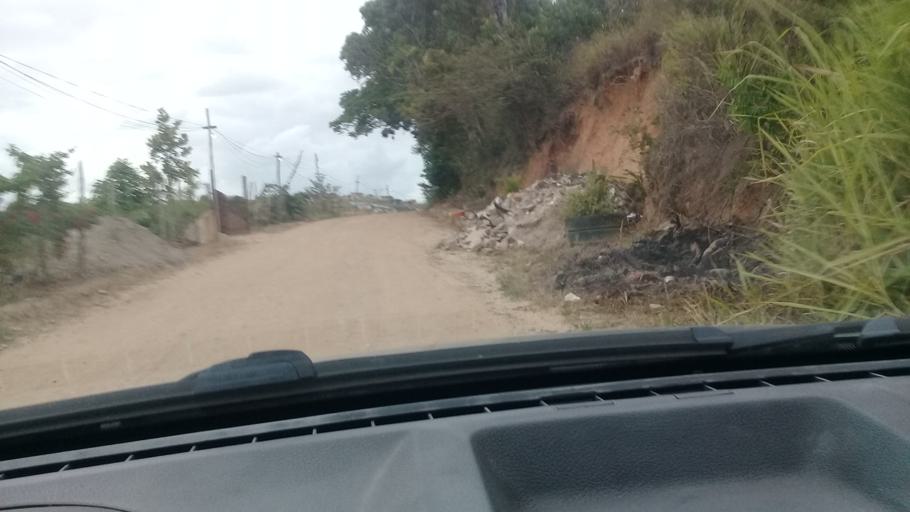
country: BR
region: Pernambuco
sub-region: Jaboatao Dos Guararapes
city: Jaboatao dos Guararapes
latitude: -8.0842
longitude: -35.0331
